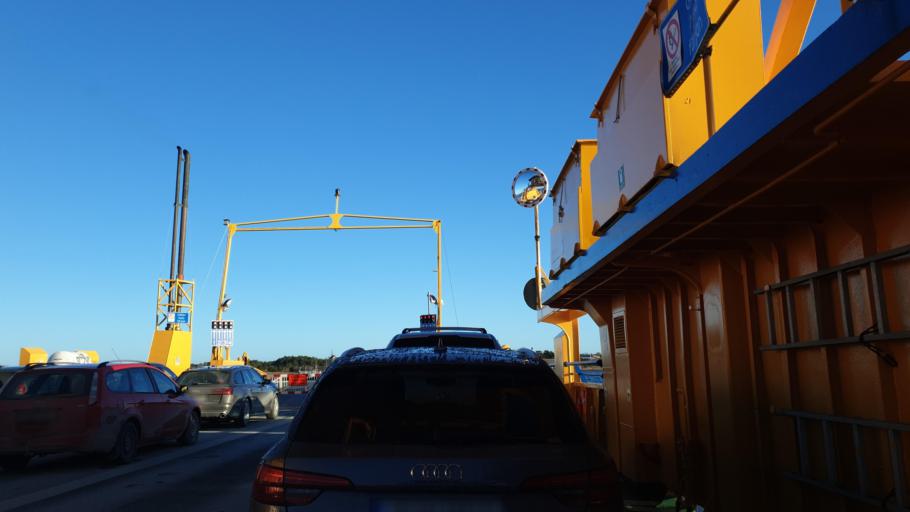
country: SE
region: Gotland
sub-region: Gotland
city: Slite
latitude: 57.8675
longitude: 19.0754
